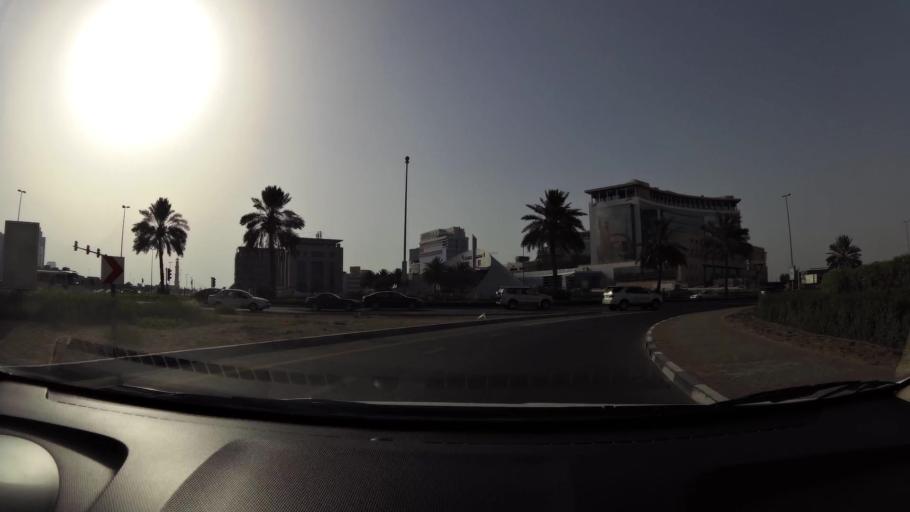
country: AE
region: Ash Shariqah
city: Sharjah
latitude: 25.2319
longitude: 55.3564
